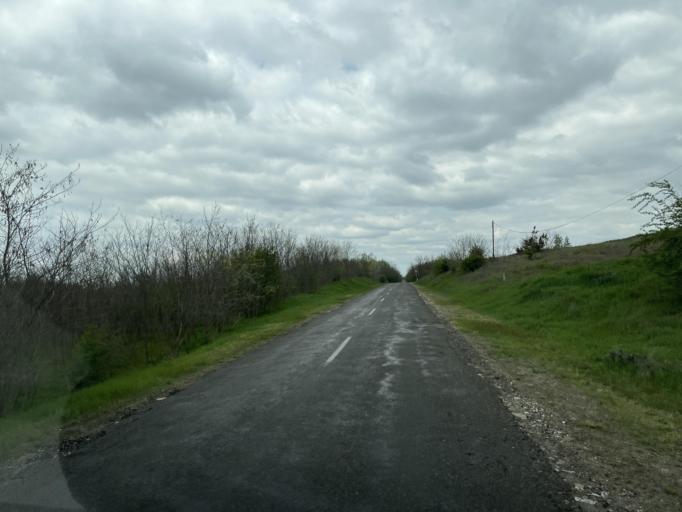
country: HU
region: Pest
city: Orkeny
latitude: 47.1080
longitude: 19.3599
